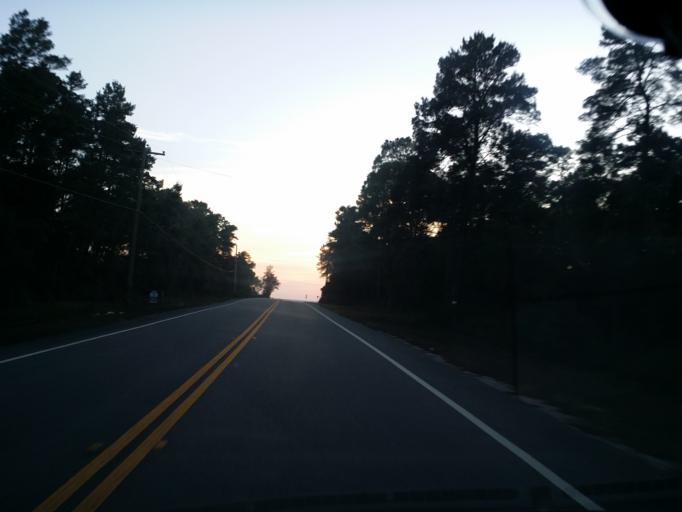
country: US
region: Florida
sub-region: Franklin County
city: Carrabelle
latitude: 29.7879
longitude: -84.7668
